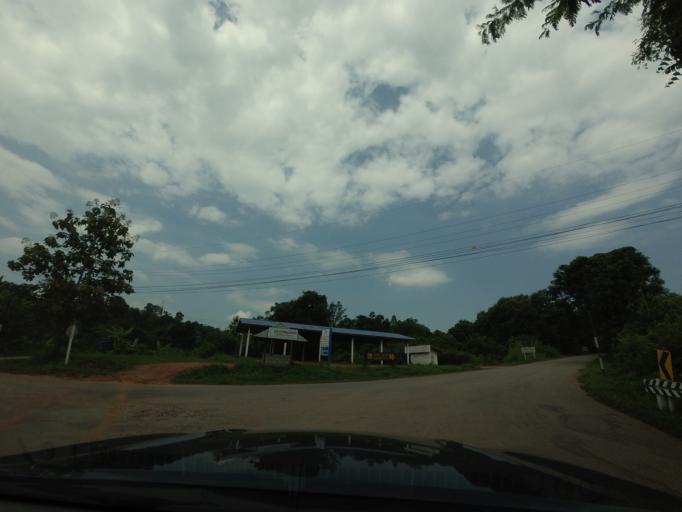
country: TH
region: Uttaradit
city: Fak Tha
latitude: 17.8117
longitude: 100.9321
